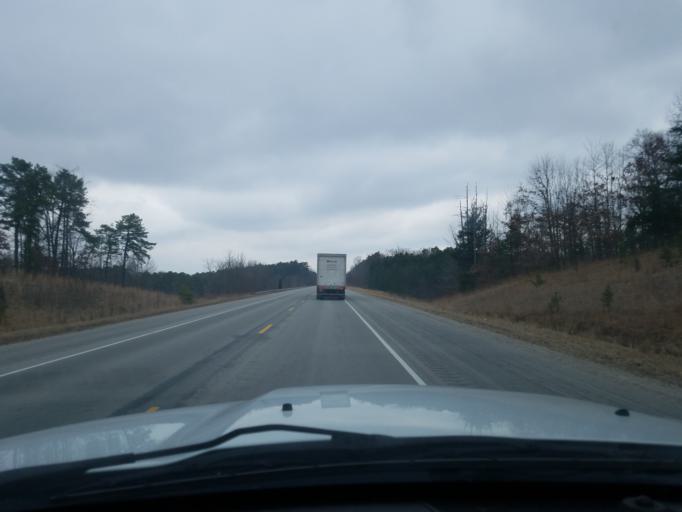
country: US
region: Indiana
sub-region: Perry County
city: Tell City
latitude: 38.0662
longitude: -86.6198
